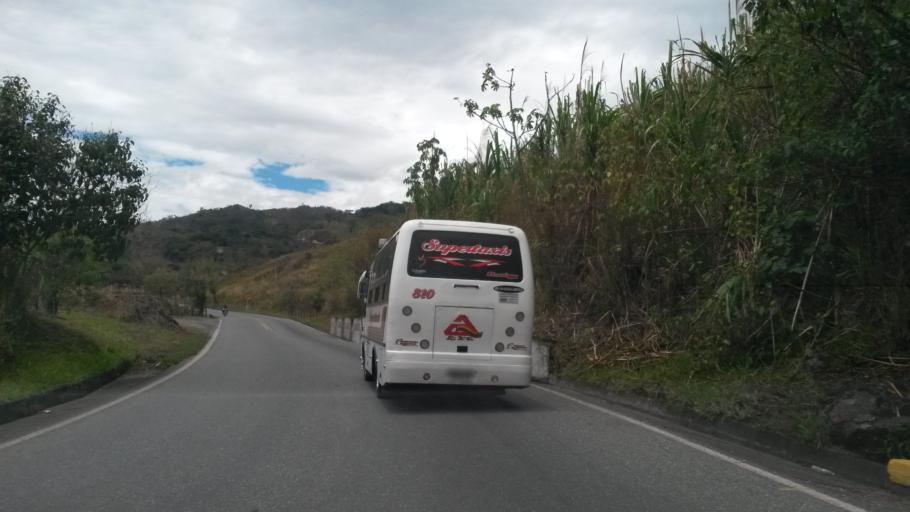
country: CO
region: Cauca
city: Rosas
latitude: 2.2773
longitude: -76.7080
